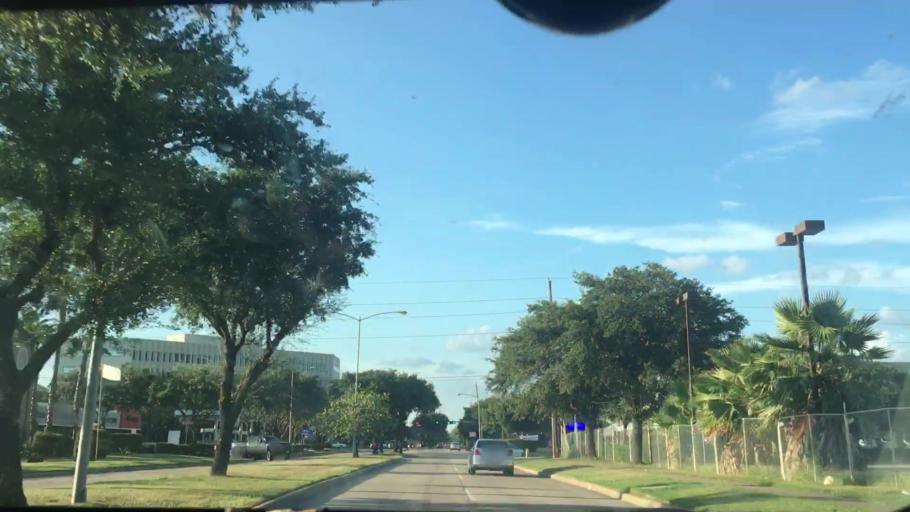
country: US
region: Texas
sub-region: Fort Bend County
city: Meadows Place
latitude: 29.6416
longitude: -95.5820
